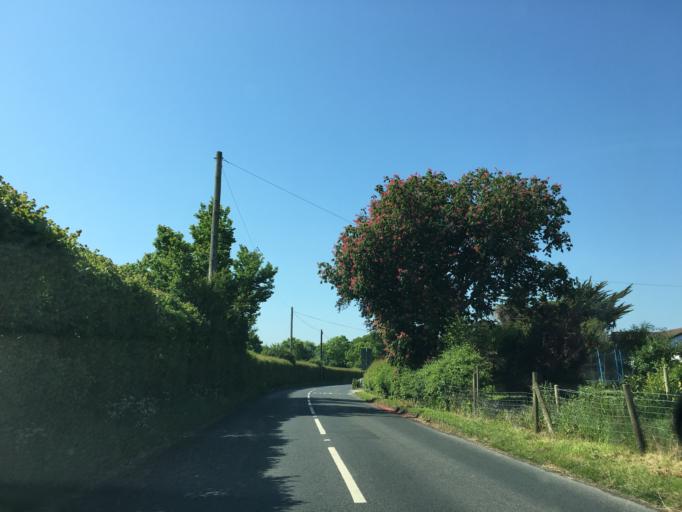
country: GB
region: England
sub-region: Isle of Wight
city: Ryde
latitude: 50.7035
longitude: -1.1670
